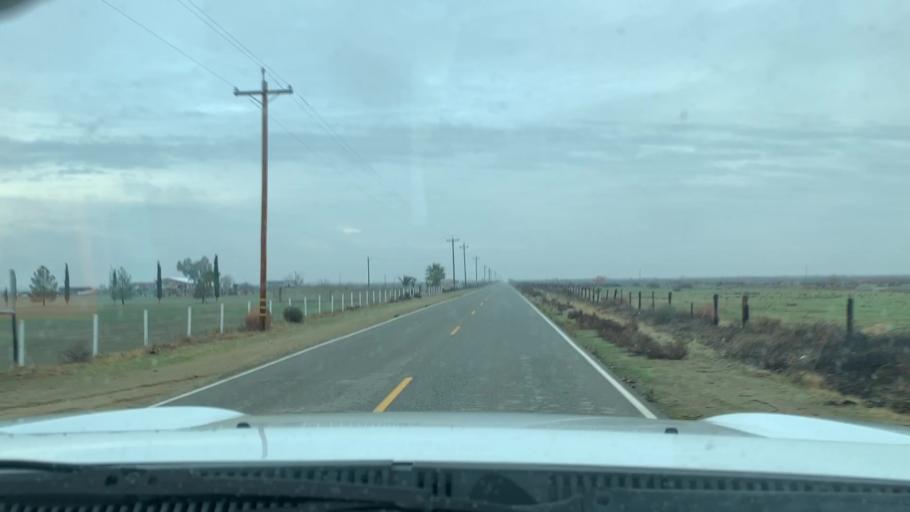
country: US
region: California
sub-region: Kern County
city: Lost Hills
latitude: 35.6975
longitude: -119.5797
